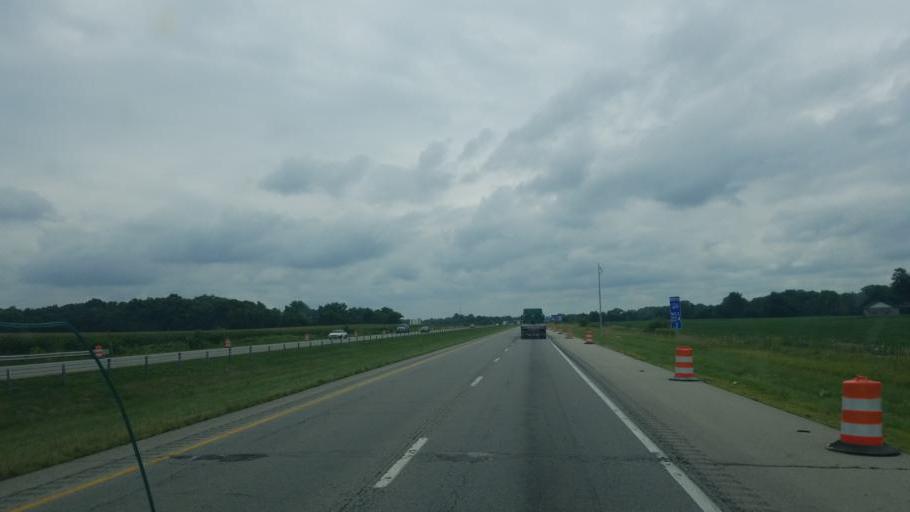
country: US
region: Indiana
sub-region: Madison County
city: Anderson
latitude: 40.0463
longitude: -85.6911
